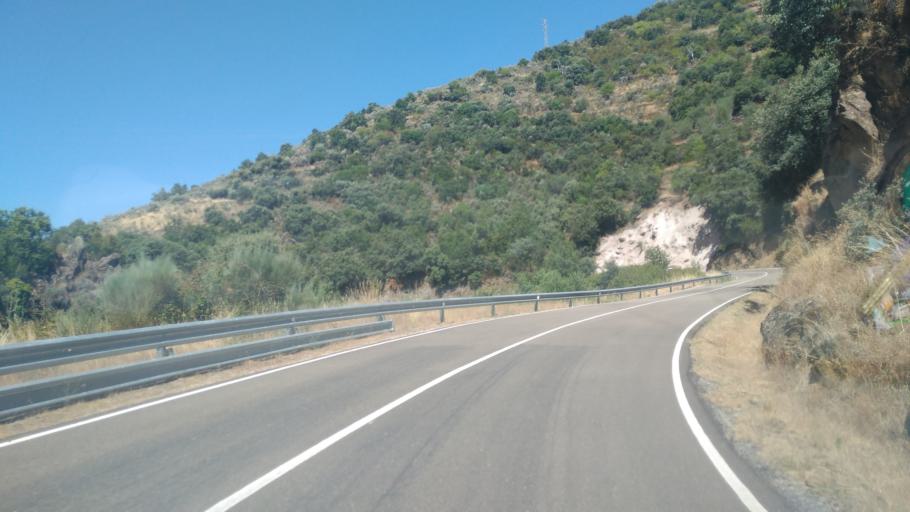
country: ES
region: Castille and Leon
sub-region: Provincia de Salamanca
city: Mieza
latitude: 41.1846
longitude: -6.6605
